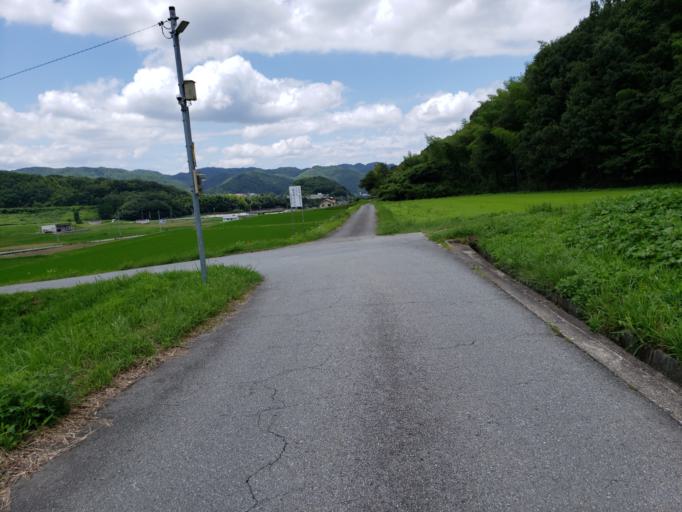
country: JP
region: Hyogo
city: Himeji
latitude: 34.8668
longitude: 134.7472
